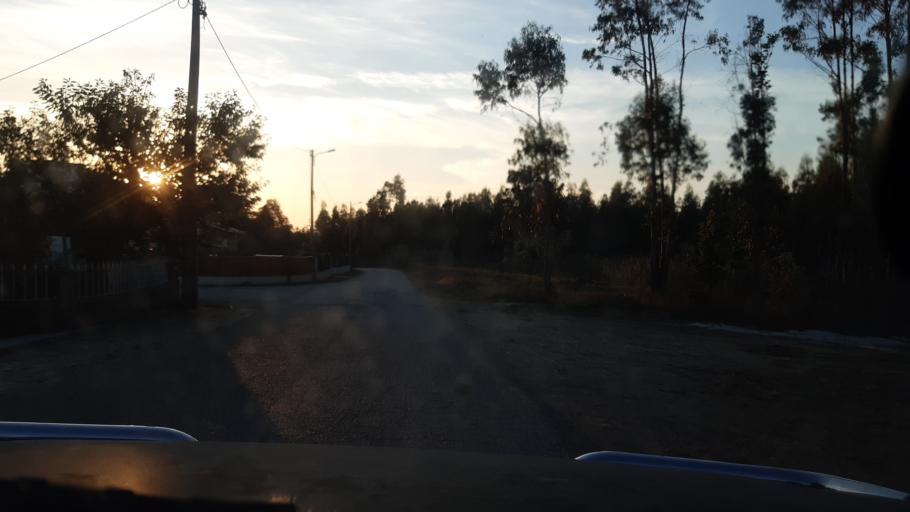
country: PT
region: Aveiro
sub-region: Agueda
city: Aguada de Cima
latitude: 40.5637
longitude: -8.3514
